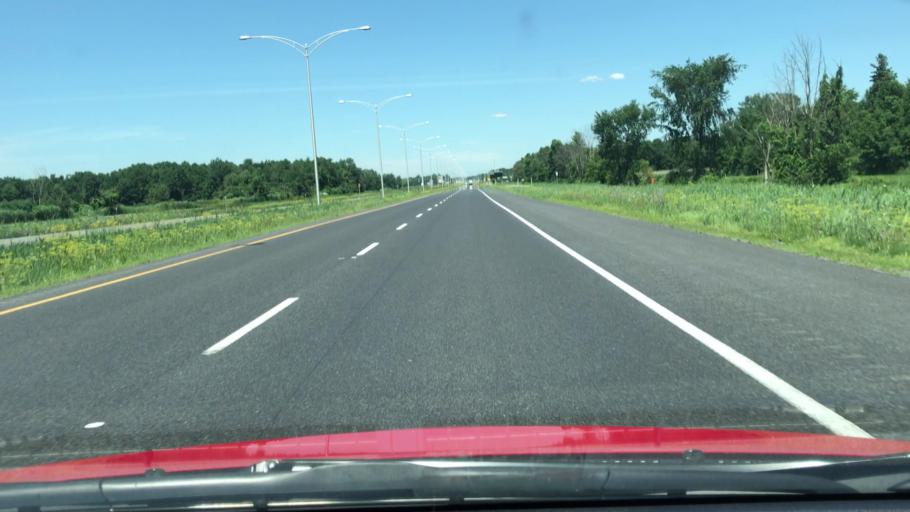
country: US
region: New York
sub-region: Clinton County
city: Champlain
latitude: 45.0262
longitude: -73.4532
